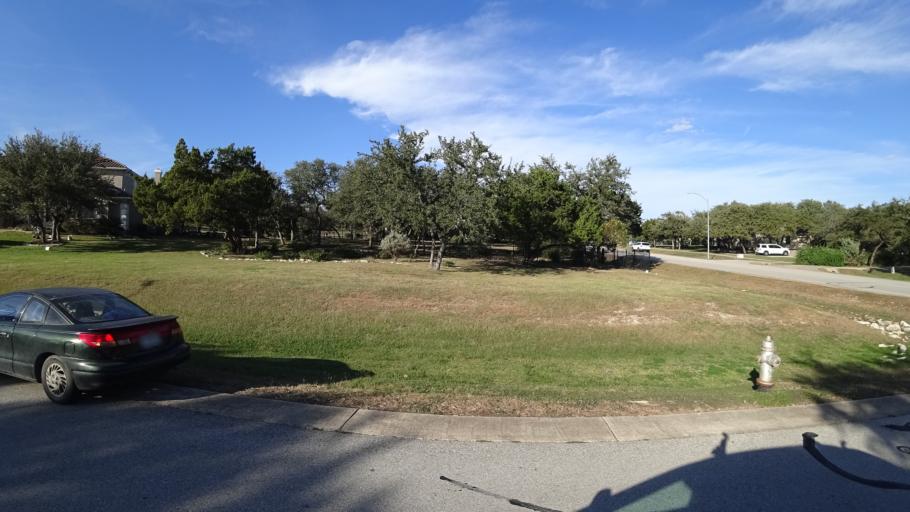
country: US
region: Texas
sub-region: Travis County
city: Barton Creek
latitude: 30.2574
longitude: -97.8445
